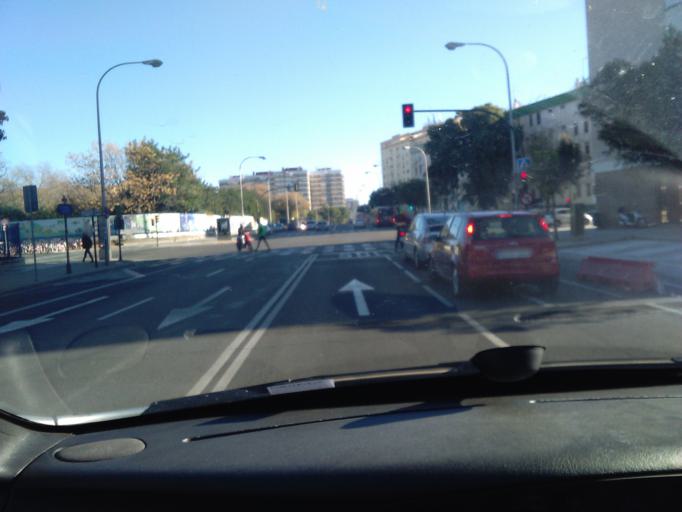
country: ES
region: Andalusia
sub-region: Provincia de Sevilla
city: Sevilla
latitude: 37.3956
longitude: -5.9647
